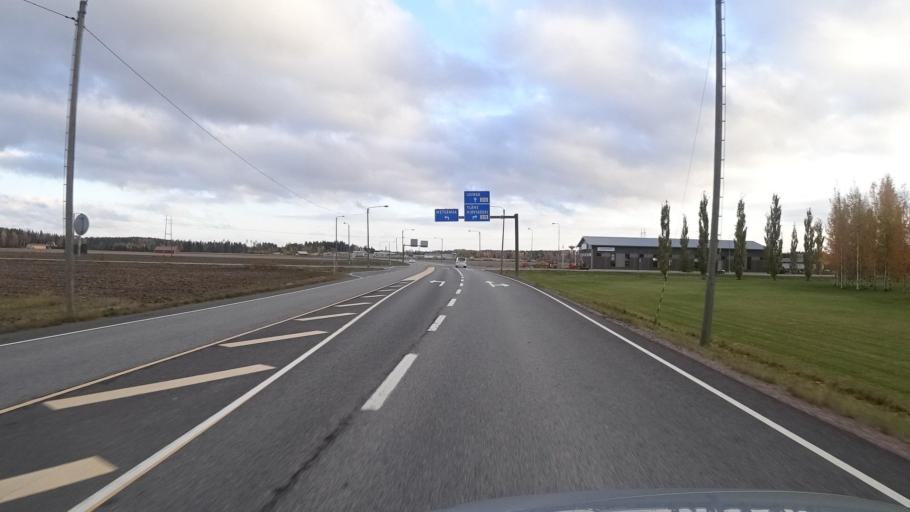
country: FI
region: Varsinais-Suomi
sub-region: Loimaa
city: Loimaa
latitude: 60.8705
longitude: 23.0021
